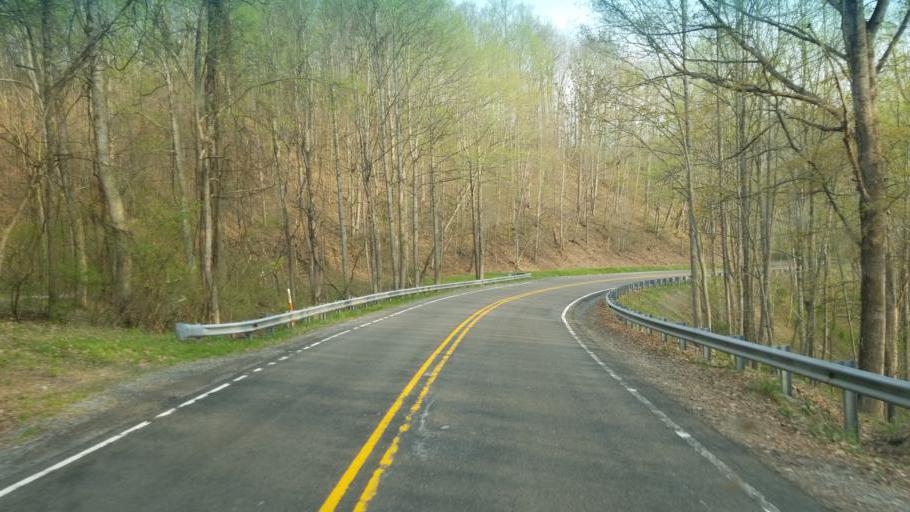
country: US
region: Virginia
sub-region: Smyth County
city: Atkins
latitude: 36.8164
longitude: -81.4275
